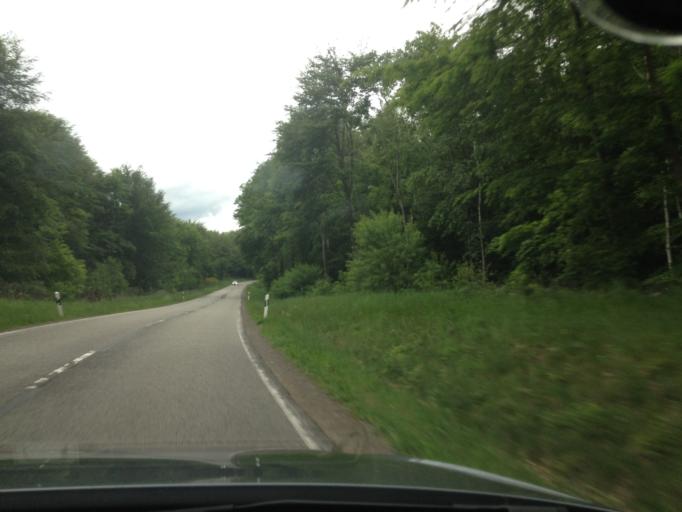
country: DE
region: Saarland
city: Neunkirchen
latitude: 49.3116
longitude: 7.1895
